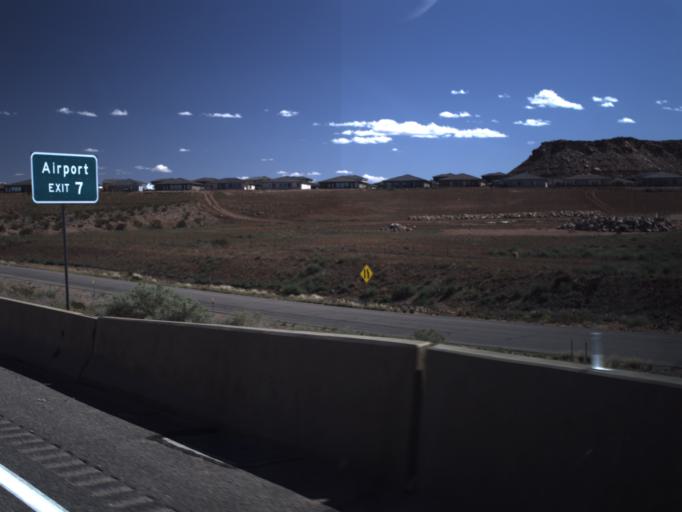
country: US
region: Utah
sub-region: Washington County
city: Saint George
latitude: 37.0089
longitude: -113.5131
